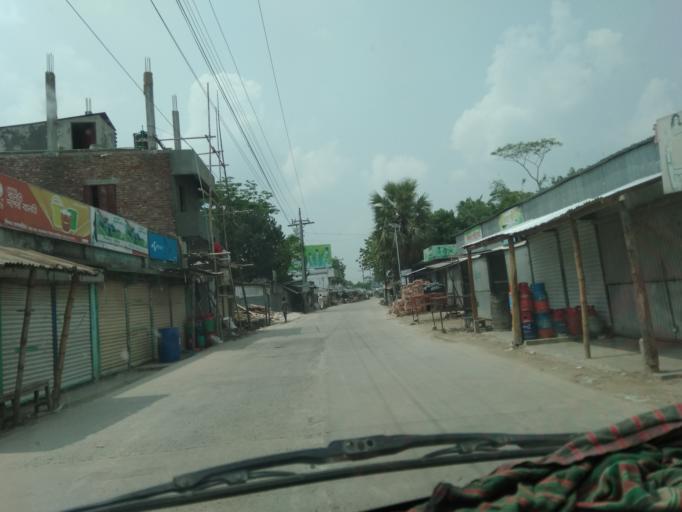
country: BD
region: Dhaka
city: Char Bhadrasan
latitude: 23.4119
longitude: 90.2146
